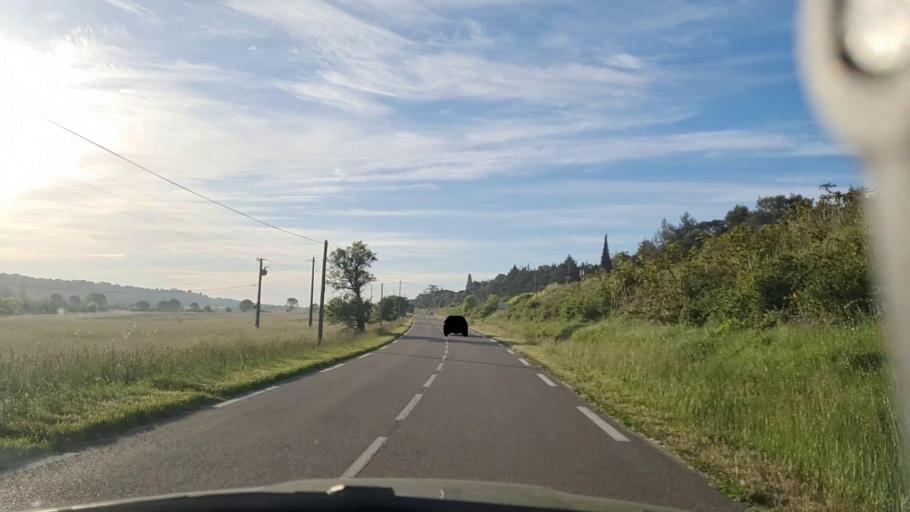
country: FR
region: Languedoc-Roussillon
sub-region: Departement du Gard
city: Caveirac
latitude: 43.8705
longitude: 4.2795
